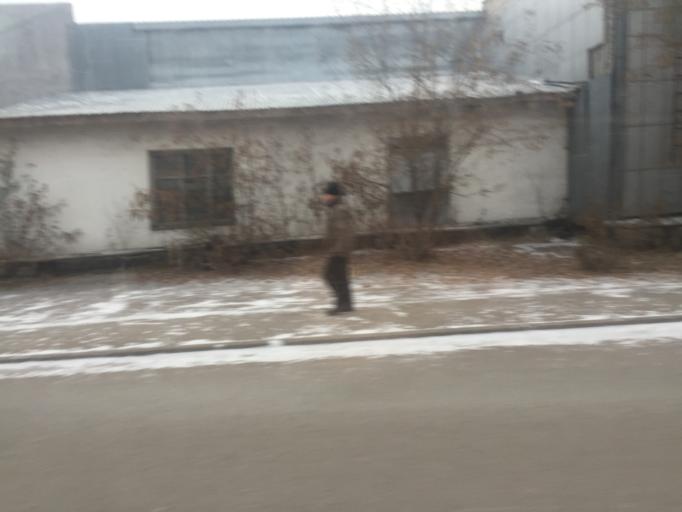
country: KZ
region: Astana Qalasy
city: Astana
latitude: 51.2012
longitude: 71.3874
